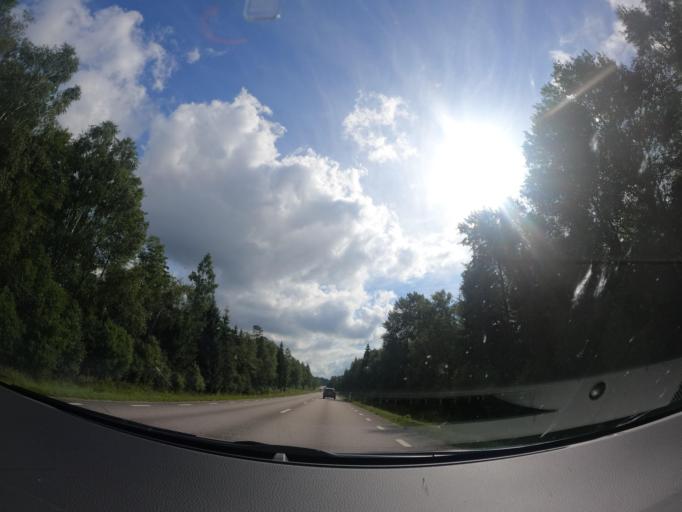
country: SE
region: Halland
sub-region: Hylte Kommun
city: Hyltebruk
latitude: 57.1276
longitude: 13.2460
